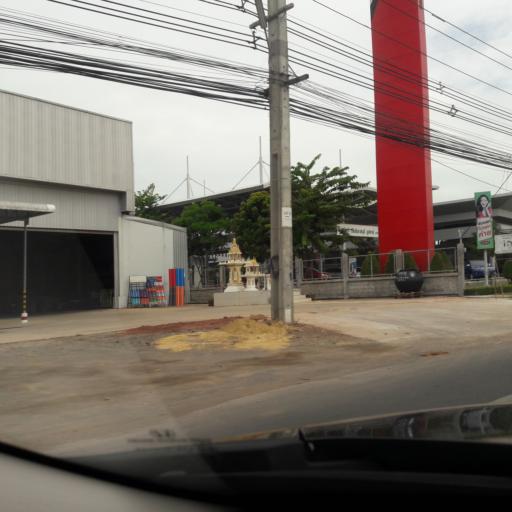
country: TH
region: Ratchaburi
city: Damnoen Saduak
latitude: 13.5481
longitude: 99.9666
